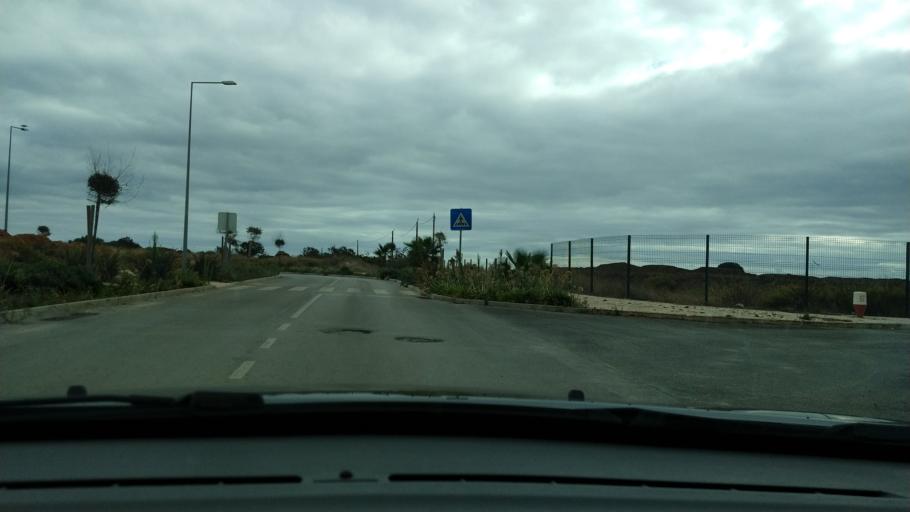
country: PT
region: Faro
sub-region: Lagos
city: Lagos
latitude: 37.0865
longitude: -8.6734
